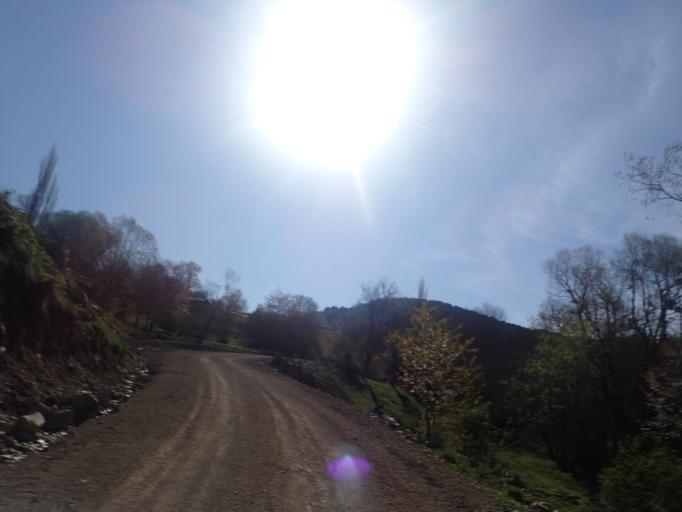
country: TR
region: Ordu
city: Mesudiye
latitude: 40.4186
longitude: 37.8328
